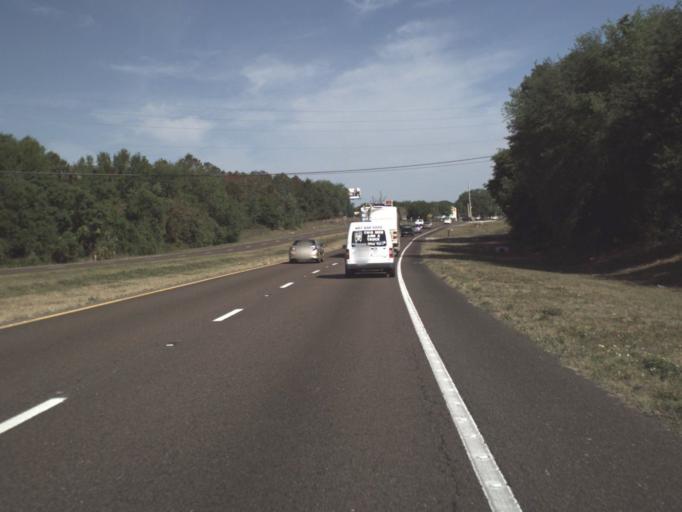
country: US
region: Florida
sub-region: Lake County
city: Hawthorne
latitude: 28.7426
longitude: -81.8746
